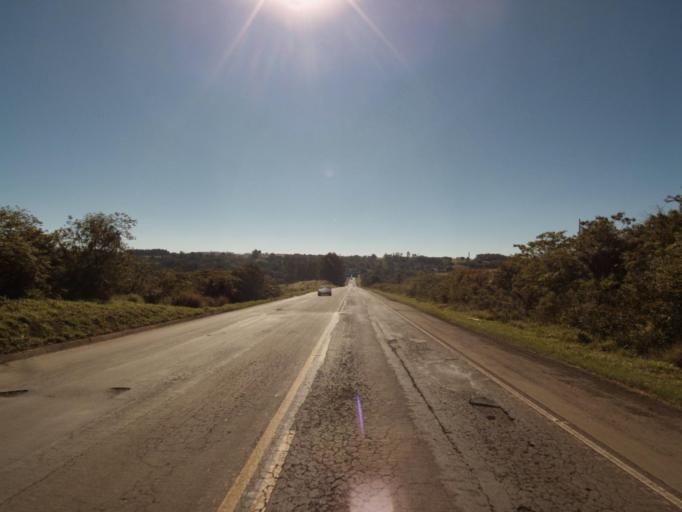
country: BR
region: Santa Catarina
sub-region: Sao Lourenco Do Oeste
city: Sao Lourenco dOeste
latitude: -26.8128
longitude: -53.1823
